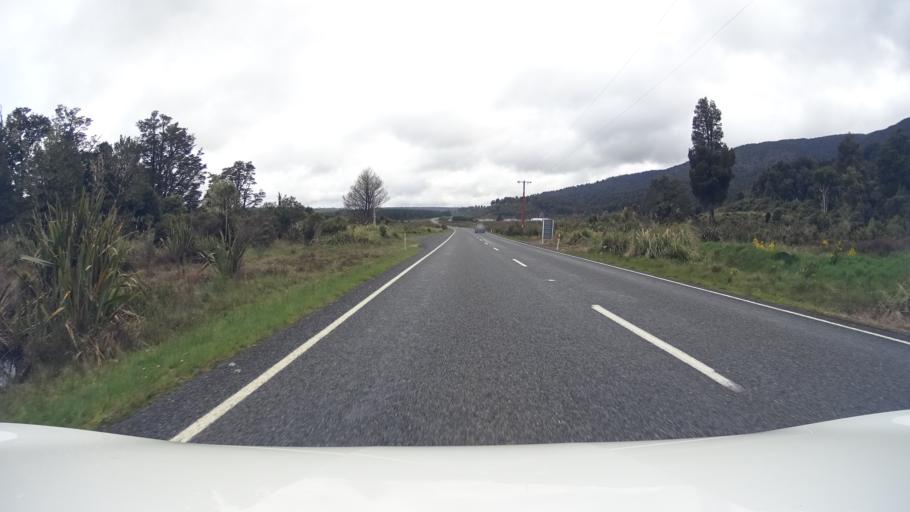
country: NZ
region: Manawatu-Wanganui
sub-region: Ruapehu District
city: Waiouru
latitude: -39.2342
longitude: 175.3926
